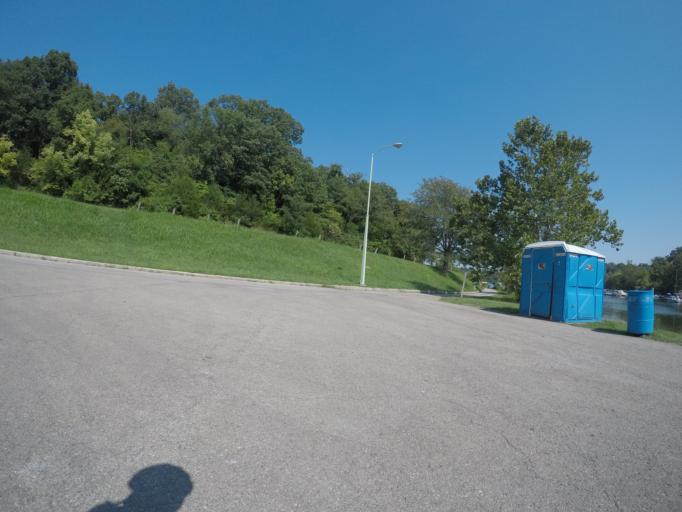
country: US
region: Kansas
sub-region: Wyandotte County
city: Edwardsville
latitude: 39.1658
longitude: -94.7886
